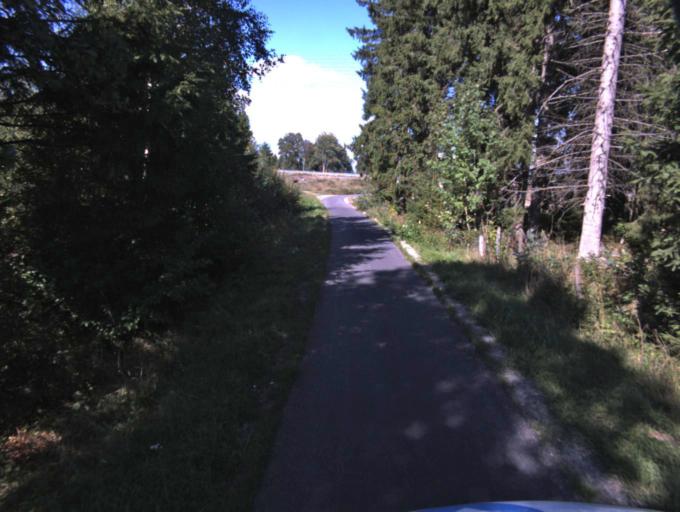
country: SE
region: Vaestra Goetaland
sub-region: Ulricehamns Kommun
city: Ulricehamn
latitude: 57.8142
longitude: 13.3542
